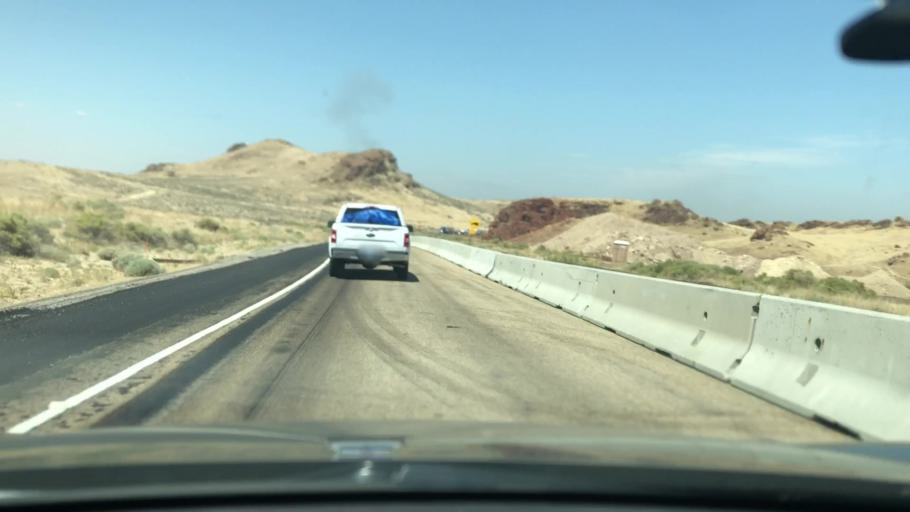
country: US
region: Idaho
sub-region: Owyhee County
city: Marsing
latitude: 43.4570
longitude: -116.8638
